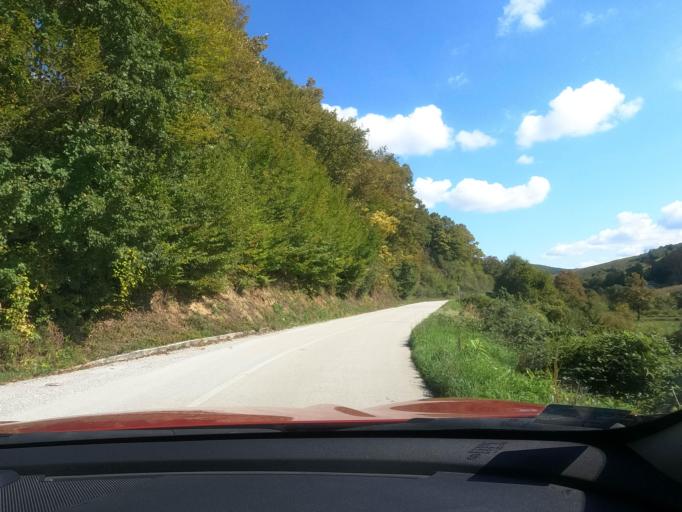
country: BA
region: Federation of Bosnia and Herzegovina
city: Velika Kladusa
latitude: 45.2042
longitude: 15.8031
